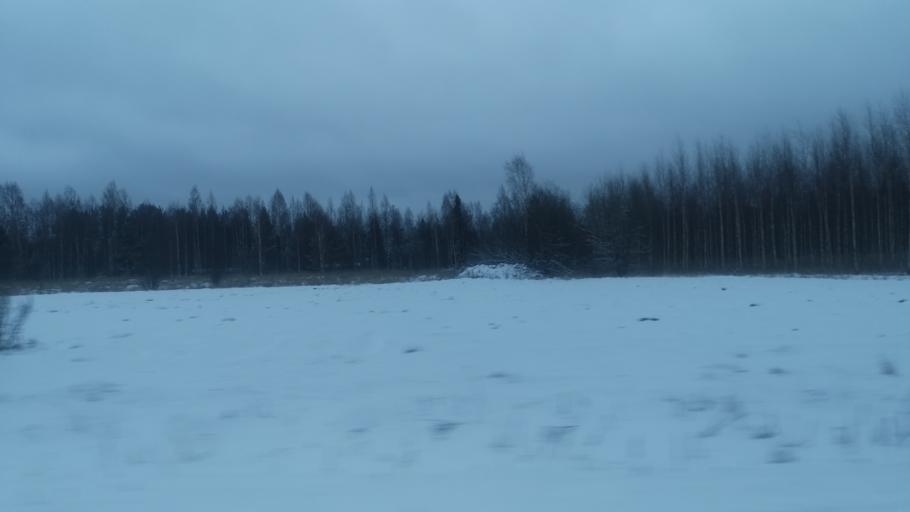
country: FI
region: Southern Savonia
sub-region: Savonlinna
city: Enonkoski
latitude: 62.0358
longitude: 28.7134
